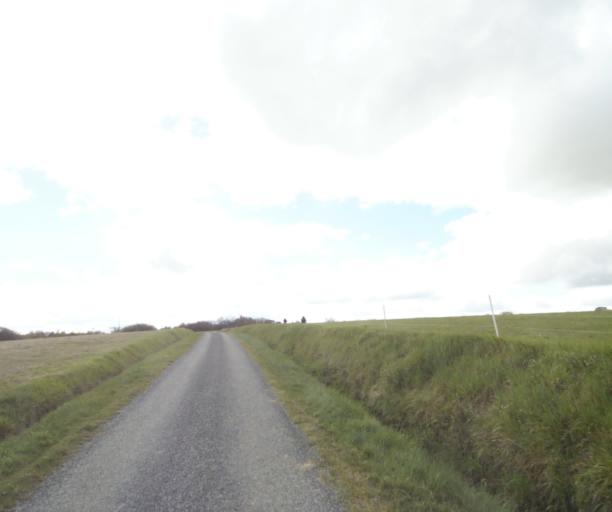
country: FR
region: Midi-Pyrenees
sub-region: Departement de l'Ariege
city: Saverdun
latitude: 43.1828
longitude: 1.5784
